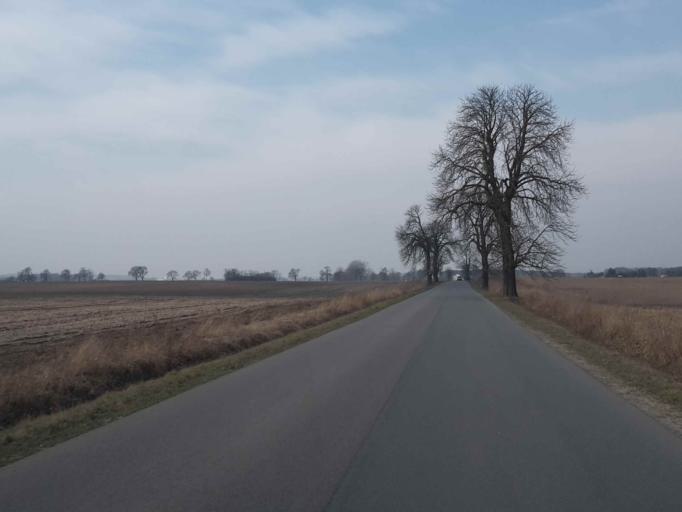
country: PL
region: Kujawsko-Pomorskie
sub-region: Powiat nakielski
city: Szubin
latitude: 53.0805
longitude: 17.7840
